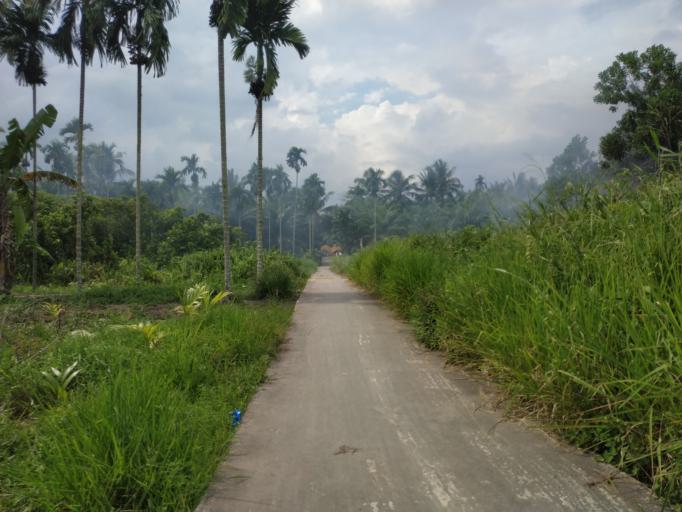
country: ID
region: Riau
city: Sungaisalak
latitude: -0.5164
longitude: 103.0030
